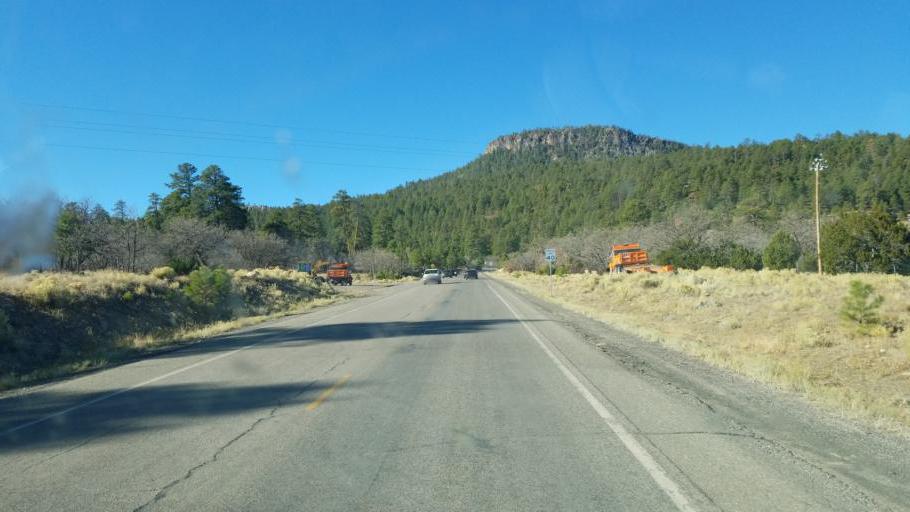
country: US
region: New Mexico
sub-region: McKinley County
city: Navajo
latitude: 36.0959
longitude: -108.8354
